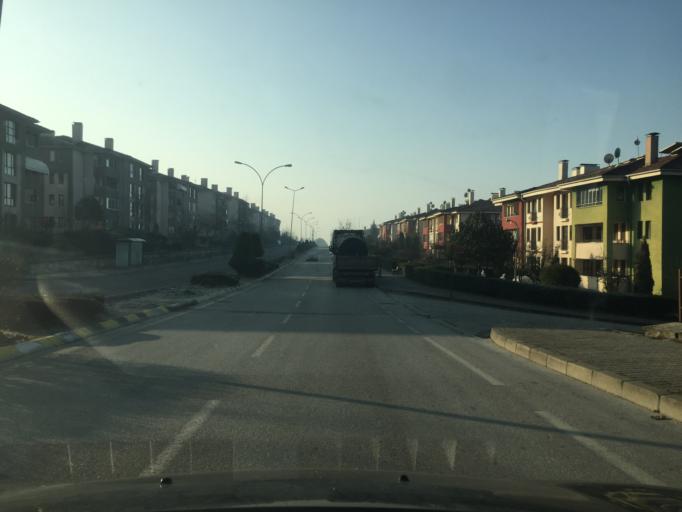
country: TR
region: Duzce
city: Duzce
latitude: 40.8658
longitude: 31.2304
